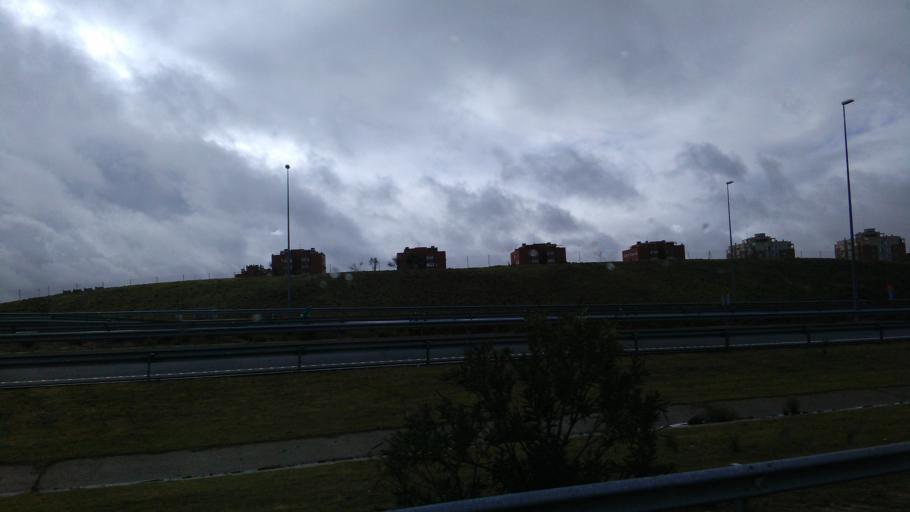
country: ES
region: Madrid
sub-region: Provincia de Madrid
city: Mostoles
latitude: 40.3069
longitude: -3.8366
